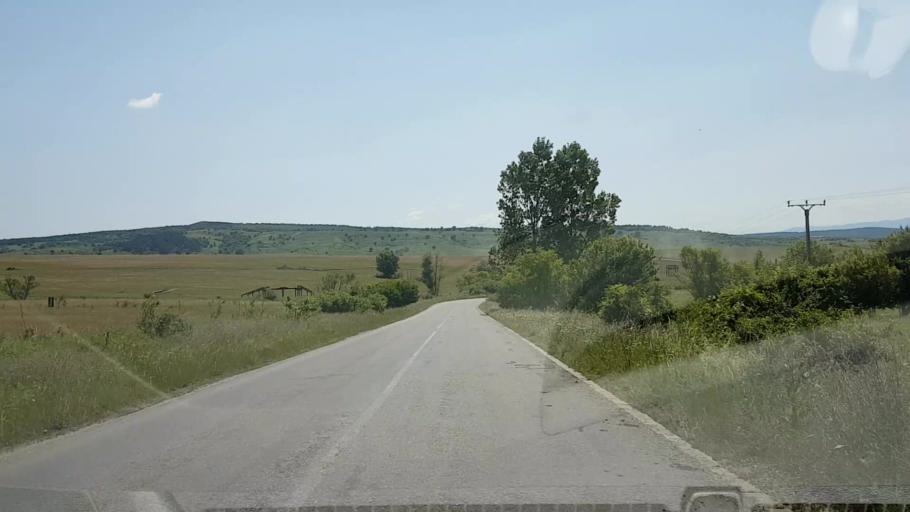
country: RO
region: Brasov
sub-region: Comuna Cincu
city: Cincu
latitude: 45.9330
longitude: 24.7933
